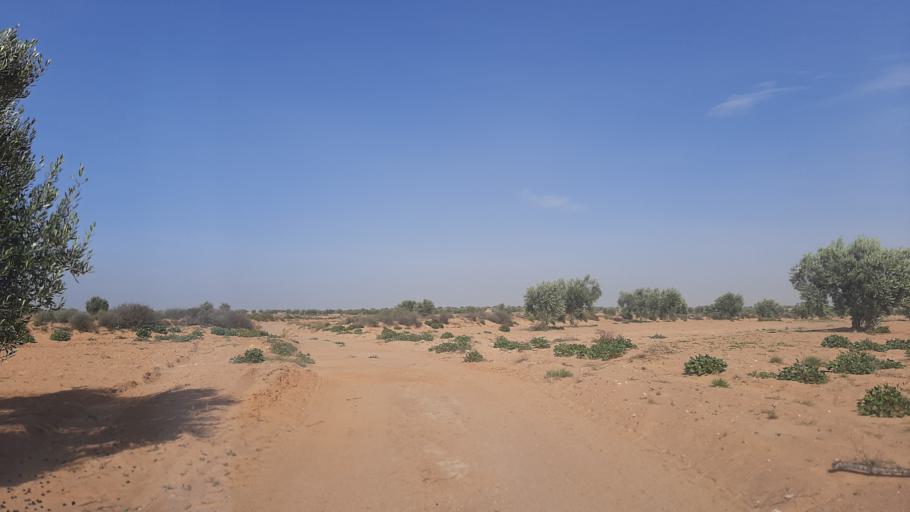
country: TN
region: Madanin
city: Zarzis
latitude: 33.4525
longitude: 10.8086
